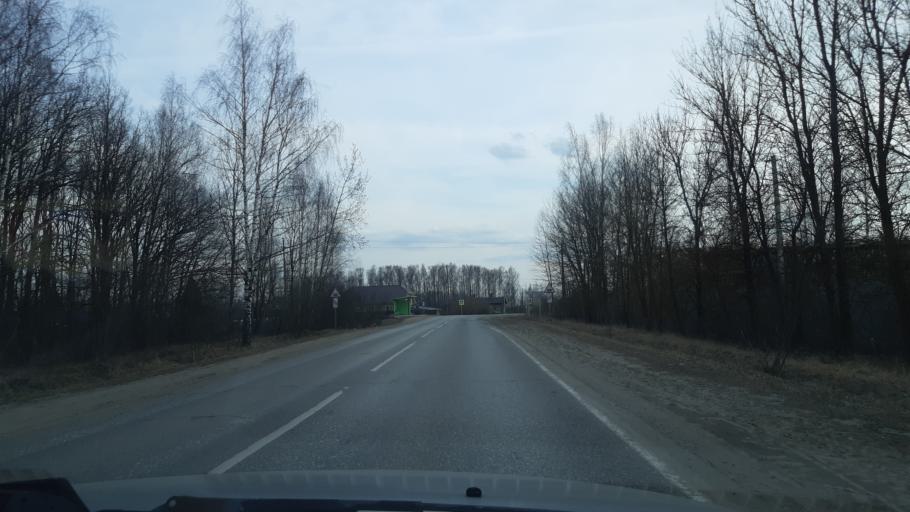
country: RU
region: Vladimir
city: Luknovo
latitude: 56.2249
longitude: 42.0348
